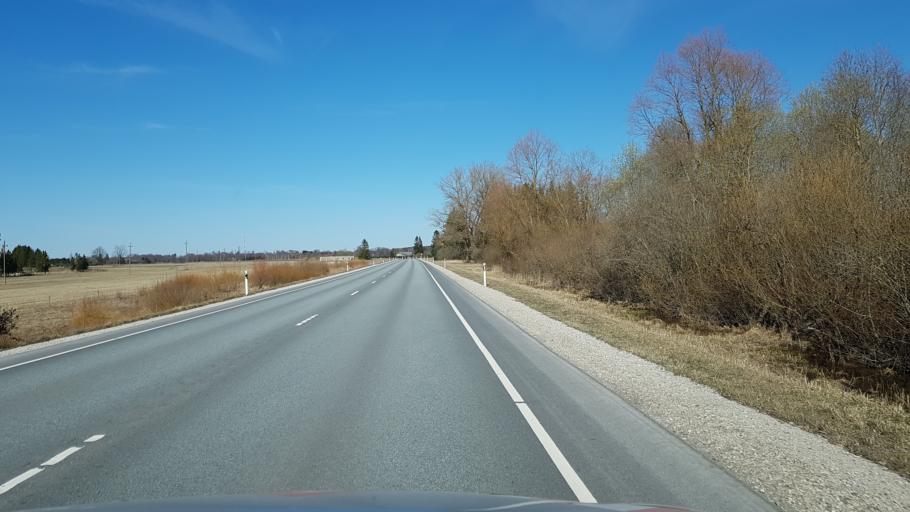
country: EE
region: Harju
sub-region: Nissi vald
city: Turba
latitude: 58.8699
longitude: 24.0821
